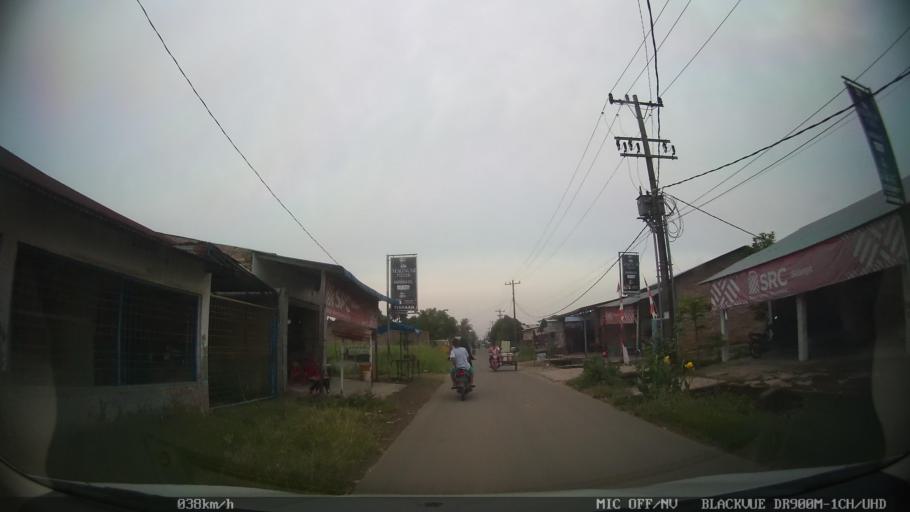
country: ID
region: North Sumatra
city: Deli Tua
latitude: 3.5455
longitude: 98.7281
